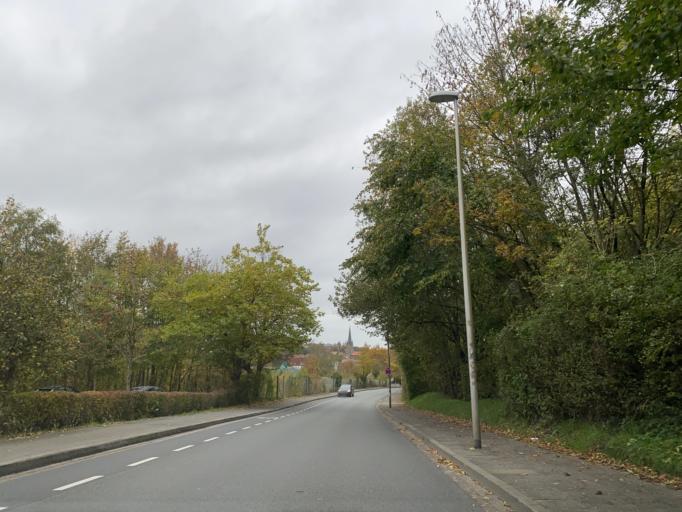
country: DE
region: Schleswig-Holstein
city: Flensburg
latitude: 54.7750
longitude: 9.4456
